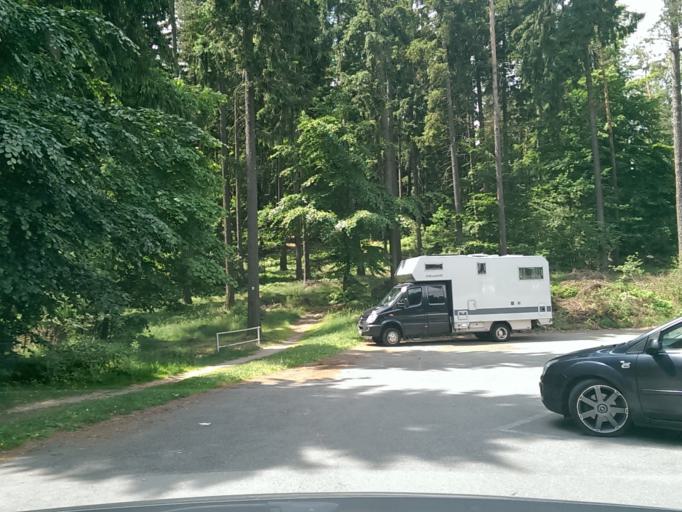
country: DE
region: Saxony
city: Kurort Jonsdorf
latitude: 50.8501
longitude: 14.6913
